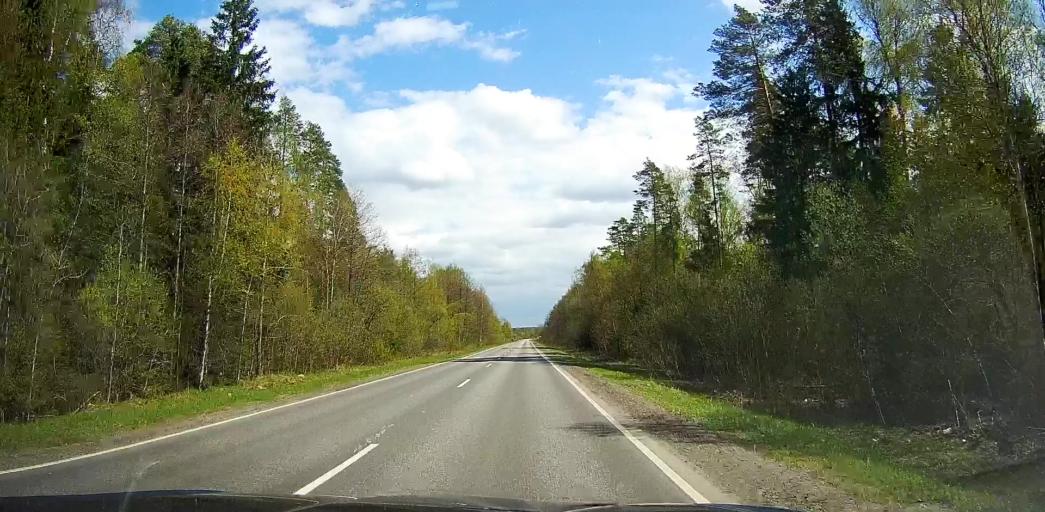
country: RU
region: Moskovskaya
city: Davydovo
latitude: 55.5513
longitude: 38.7818
